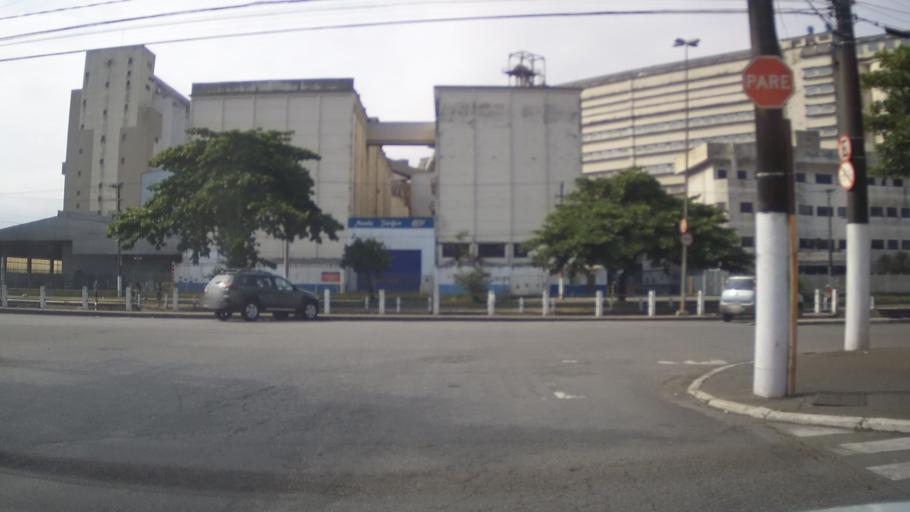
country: BR
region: Sao Paulo
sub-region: Santos
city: Santos
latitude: -23.9612
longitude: -46.3077
